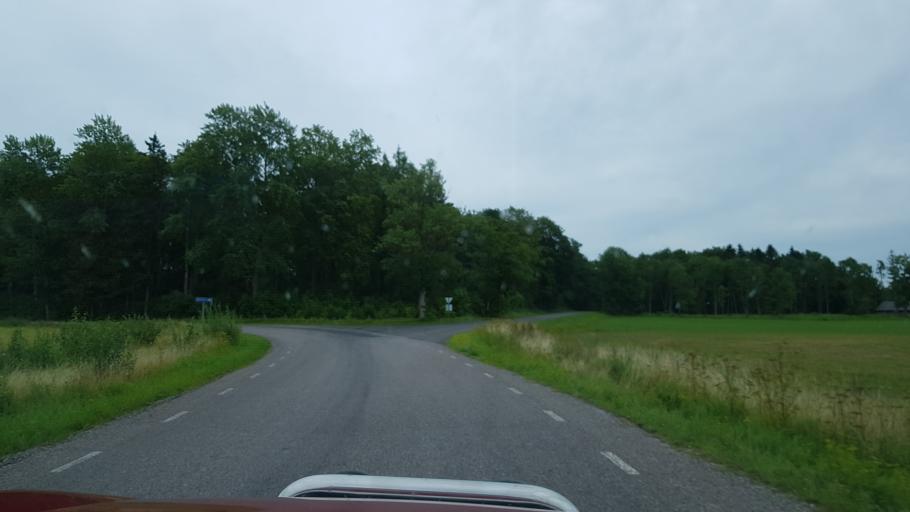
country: EE
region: Laeaene
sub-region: Lihula vald
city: Lihula
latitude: 58.8753
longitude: 23.8044
